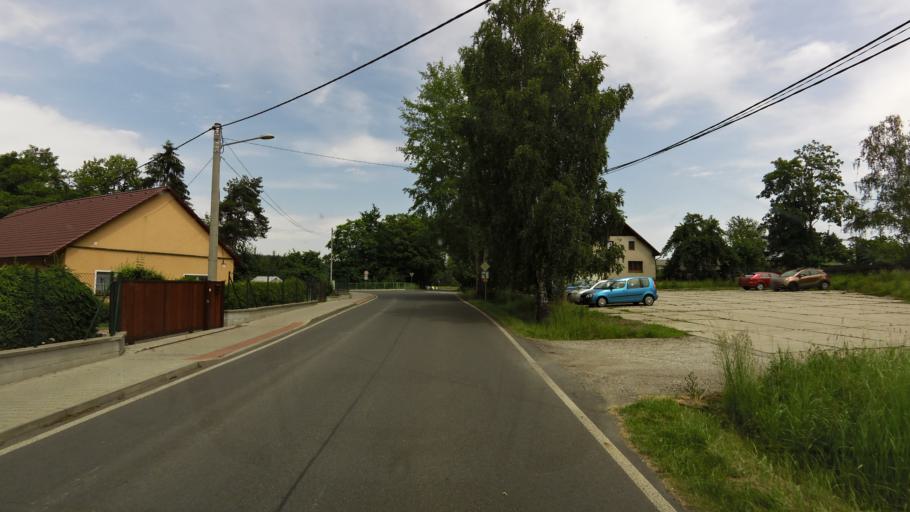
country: CZ
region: Plzensky
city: Holoubkov
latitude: 49.7726
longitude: 13.6944
